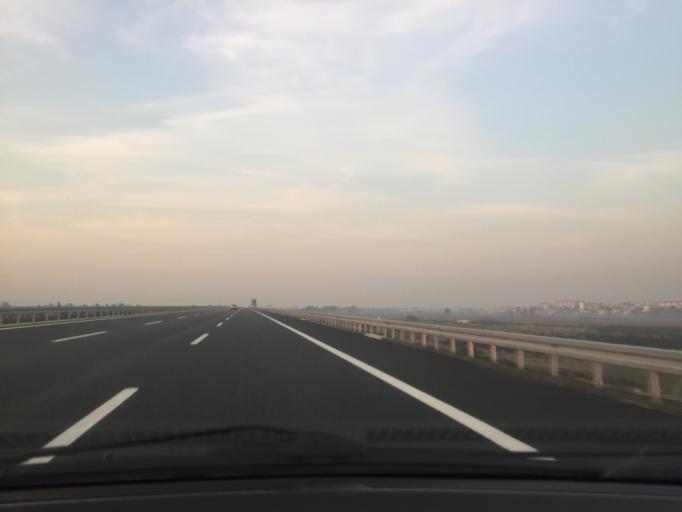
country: TR
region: Bursa
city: Karacabey
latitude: 40.2082
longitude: 28.3835
